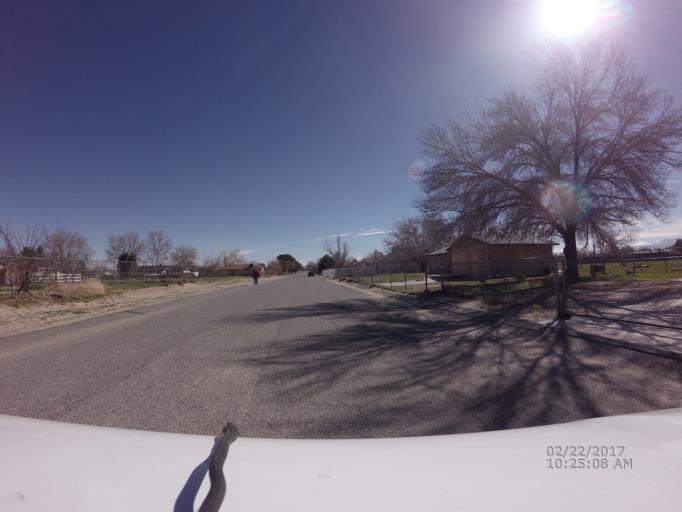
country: US
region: California
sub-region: Los Angeles County
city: Lake Los Angeles
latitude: 34.6248
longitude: -117.8250
